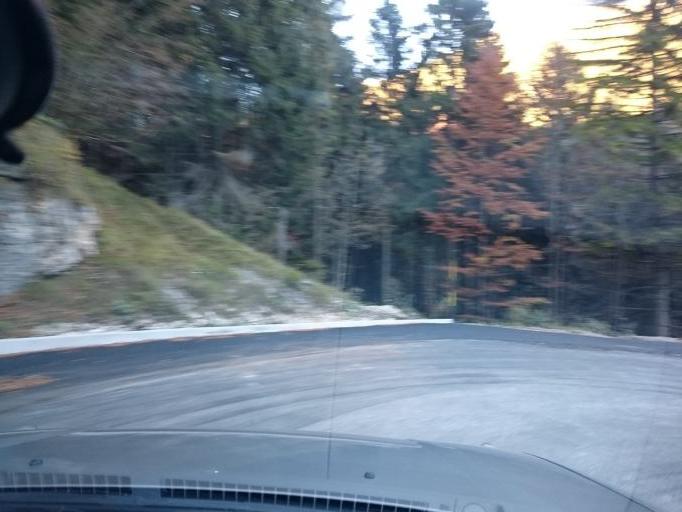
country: IT
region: Trentino-Alto Adige
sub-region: Provincia di Trento
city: Novaledo
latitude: 45.9611
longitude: 11.4264
